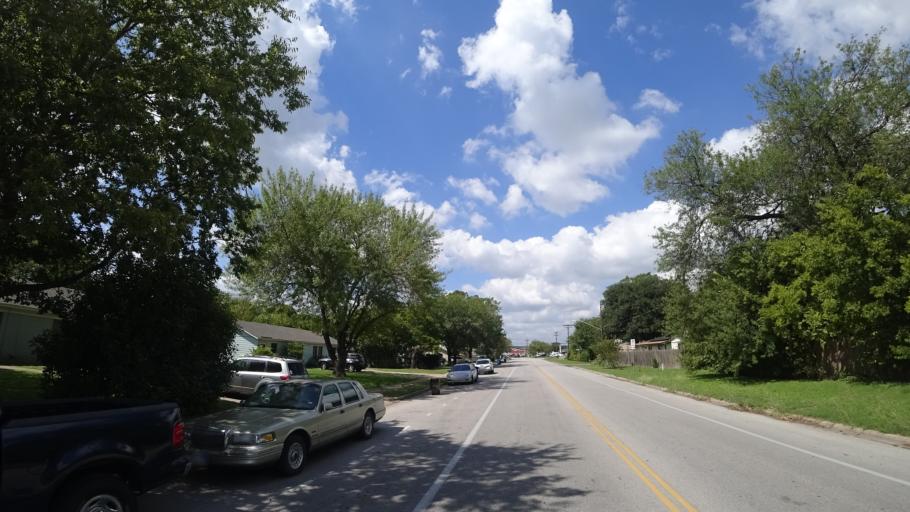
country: US
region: Texas
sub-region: Williamson County
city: Jollyville
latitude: 30.3619
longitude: -97.7266
